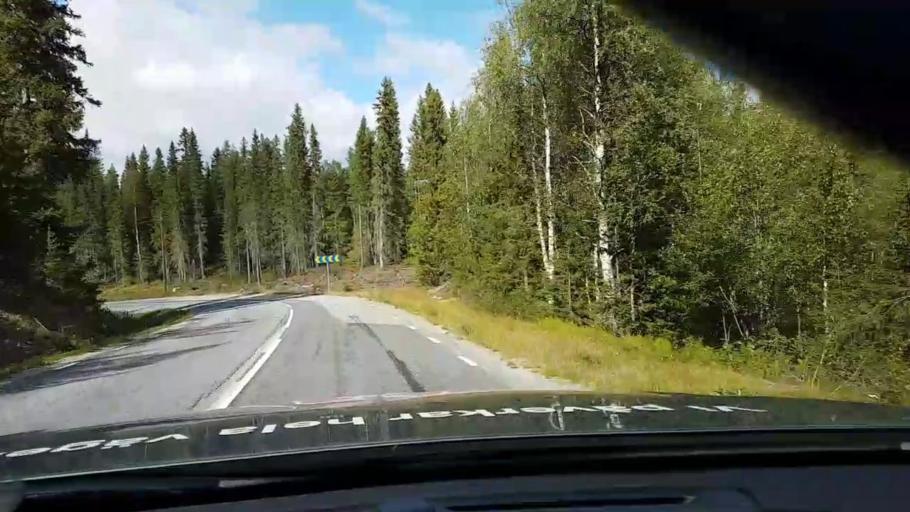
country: SE
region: Vaesterbotten
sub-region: Asele Kommun
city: Asele
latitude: 63.8441
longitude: 17.4230
